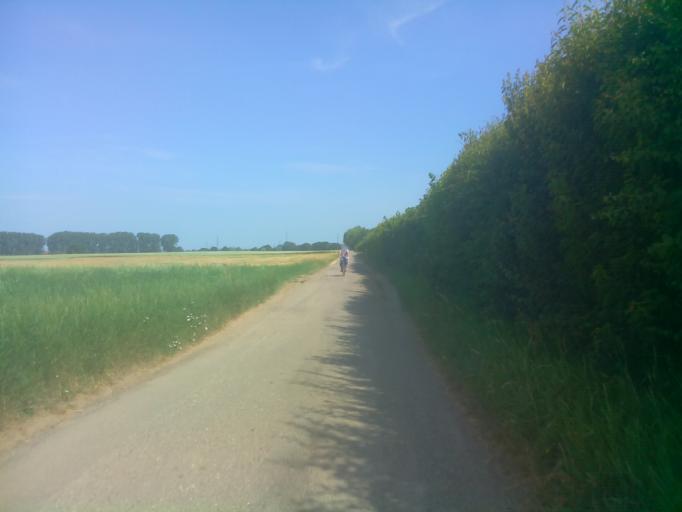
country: DE
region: Baden-Wuerttemberg
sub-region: Karlsruhe Region
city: Heddesheim
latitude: 49.5177
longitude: 8.6347
